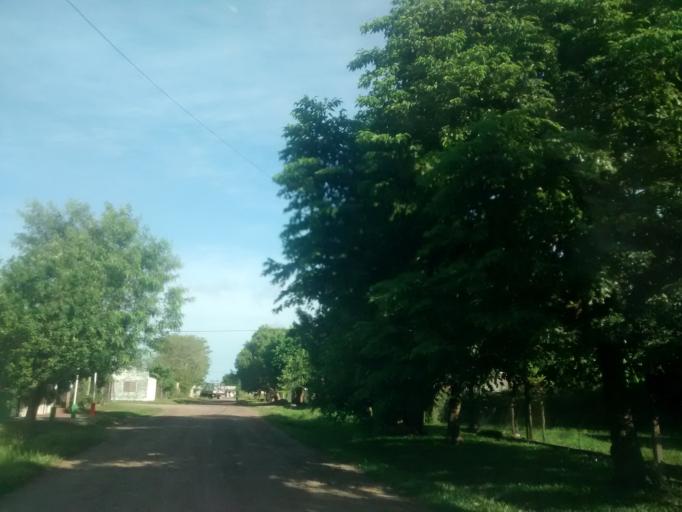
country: AR
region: Chaco
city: Puerto Tirol
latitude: -27.3746
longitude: -59.0958
